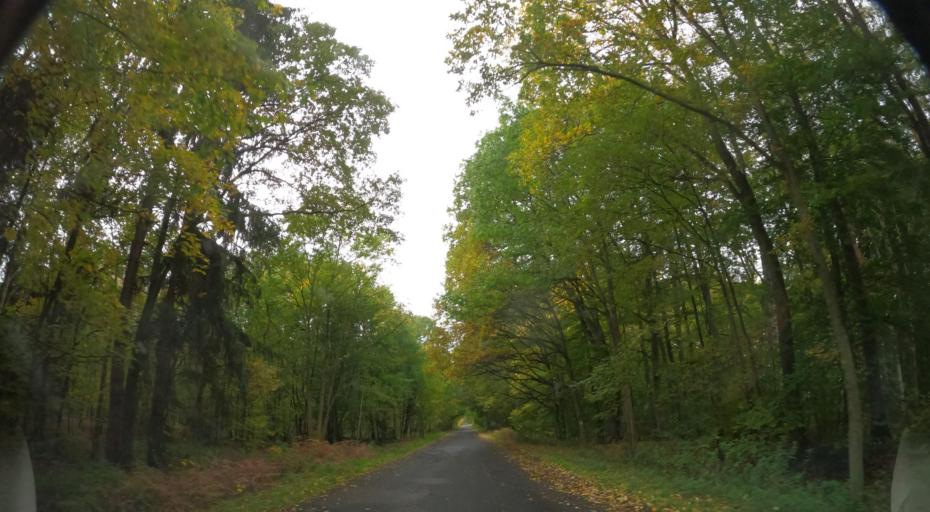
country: PL
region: West Pomeranian Voivodeship
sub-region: Powiat goleniowski
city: Stepnica
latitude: 53.6711
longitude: 14.6681
